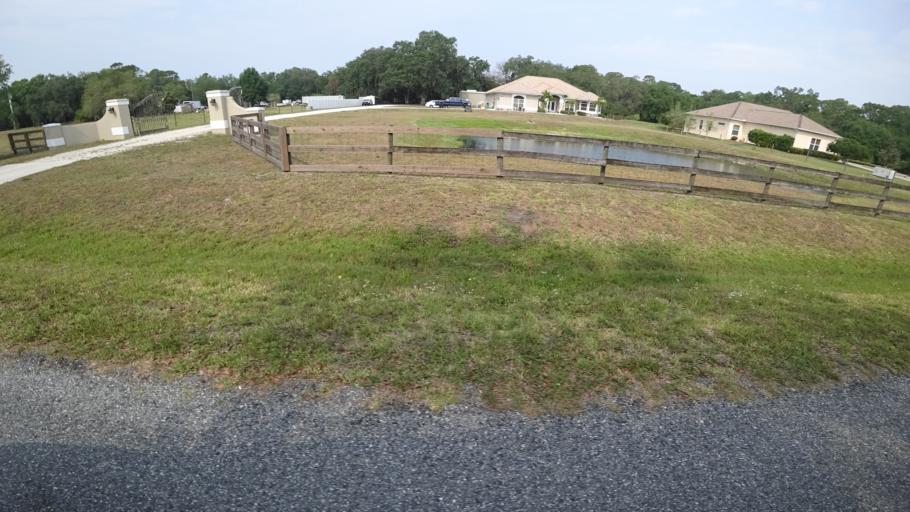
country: US
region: Florida
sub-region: Manatee County
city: Samoset
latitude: 27.4703
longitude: -82.5097
